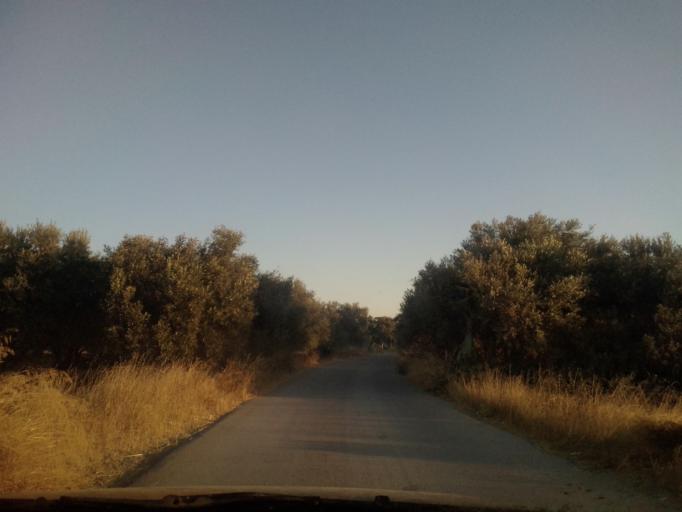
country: CY
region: Limassol
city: Ypsonas
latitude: 34.6726
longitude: 32.9687
